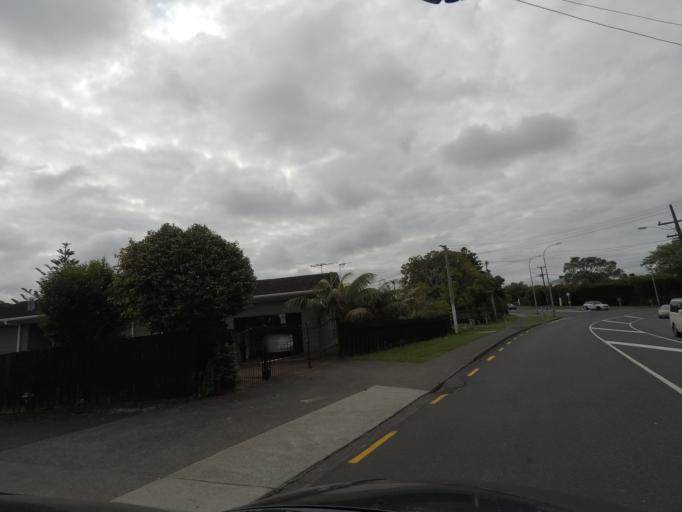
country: NZ
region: Auckland
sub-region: Auckland
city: Rosebank
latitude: -36.8439
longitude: 174.6075
